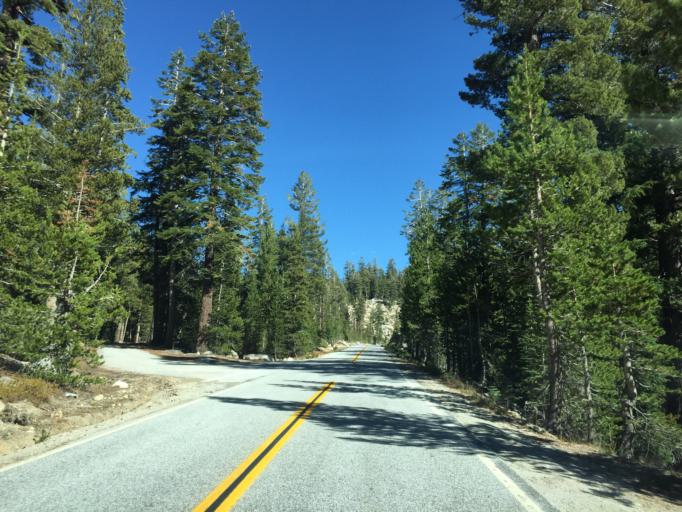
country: US
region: California
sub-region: Mariposa County
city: Yosemite Valley
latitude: 37.8172
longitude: -119.5120
